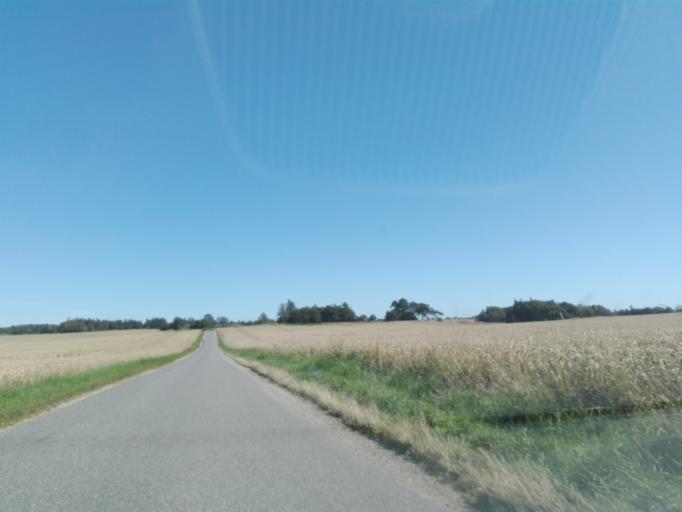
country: DK
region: Central Jutland
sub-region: Arhus Kommune
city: Malling
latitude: 55.9919
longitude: 10.2274
